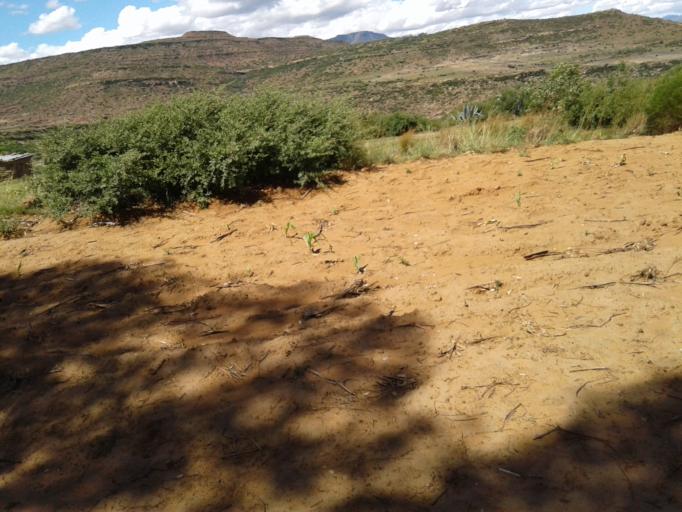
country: LS
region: Quthing
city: Quthing
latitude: -30.3697
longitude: 27.5491
